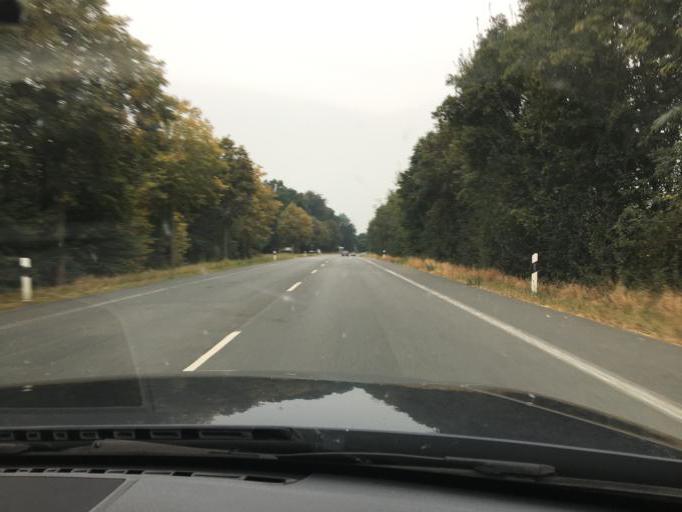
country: DE
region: North Rhine-Westphalia
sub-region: Regierungsbezirk Munster
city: Ladbergen
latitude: 52.1304
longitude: 7.7287
